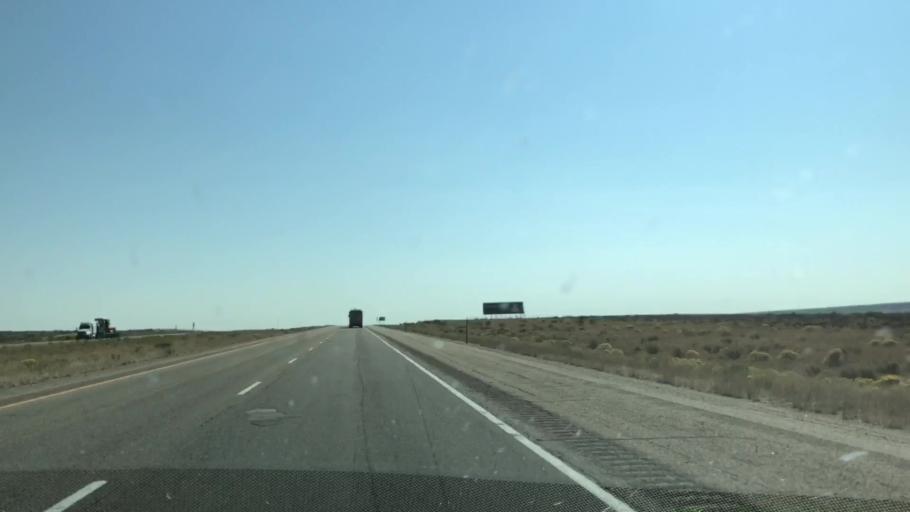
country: US
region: Wyoming
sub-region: Sweetwater County
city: Rock Springs
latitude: 41.6339
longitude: -108.3908
